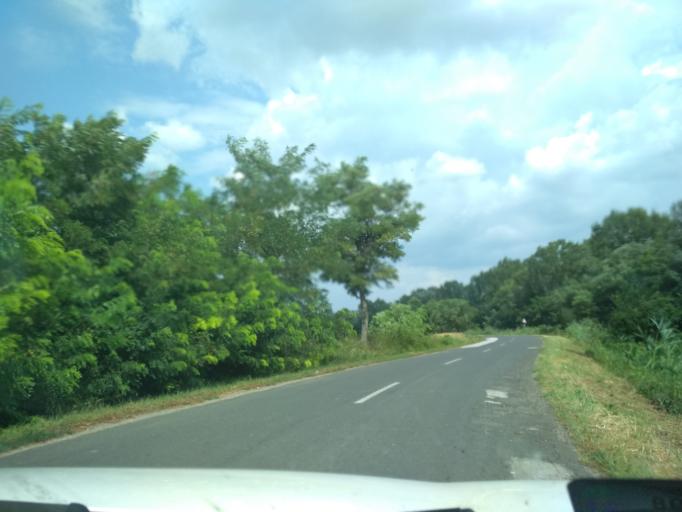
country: HU
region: Jasz-Nagykun-Szolnok
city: Tiszaszolos
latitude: 47.5242
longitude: 20.6804
